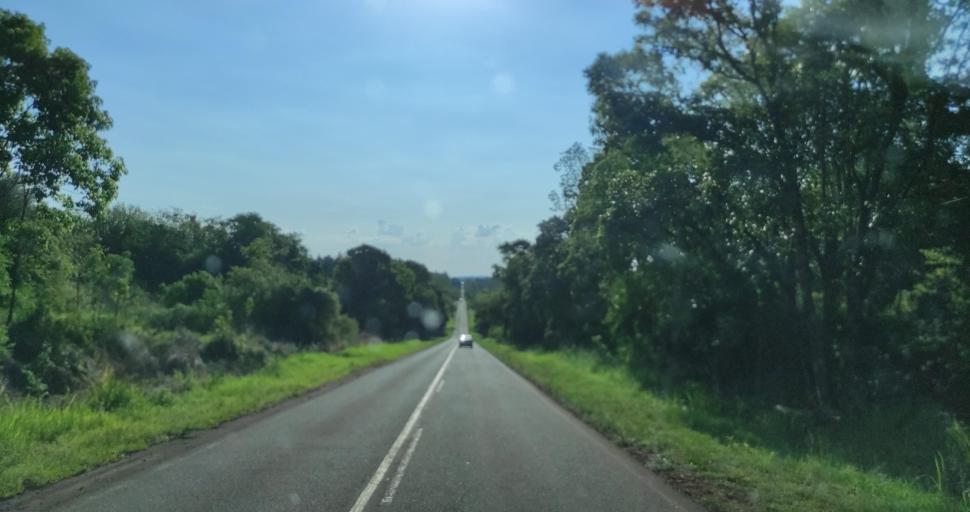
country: AR
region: Misiones
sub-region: Departamento de Eldorado
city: Eldorado
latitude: -26.3996
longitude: -54.3798
